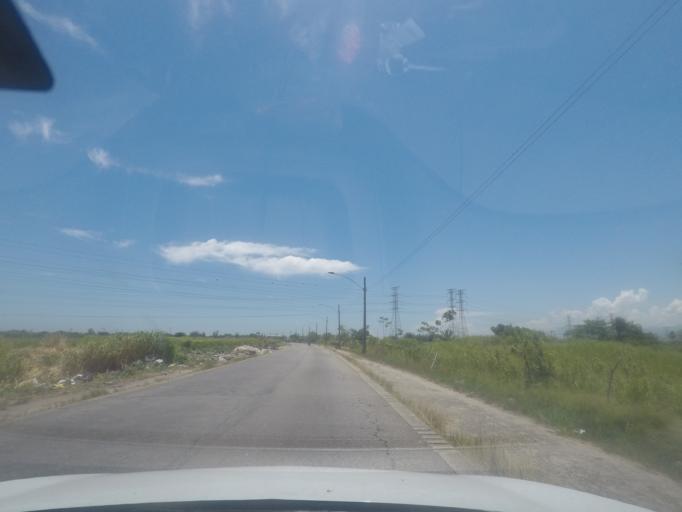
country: BR
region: Rio de Janeiro
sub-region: Itaguai
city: Itaguai
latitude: -22.8974
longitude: -43.6869
